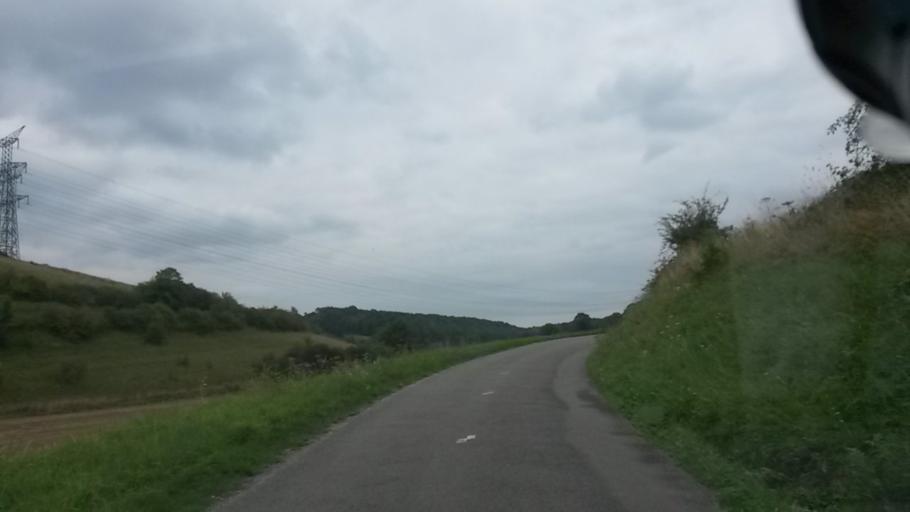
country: FR
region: Haute-Normandie
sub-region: Departement de la Seine-Maritime
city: La Feuillie
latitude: 49.4817
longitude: 1.5169
